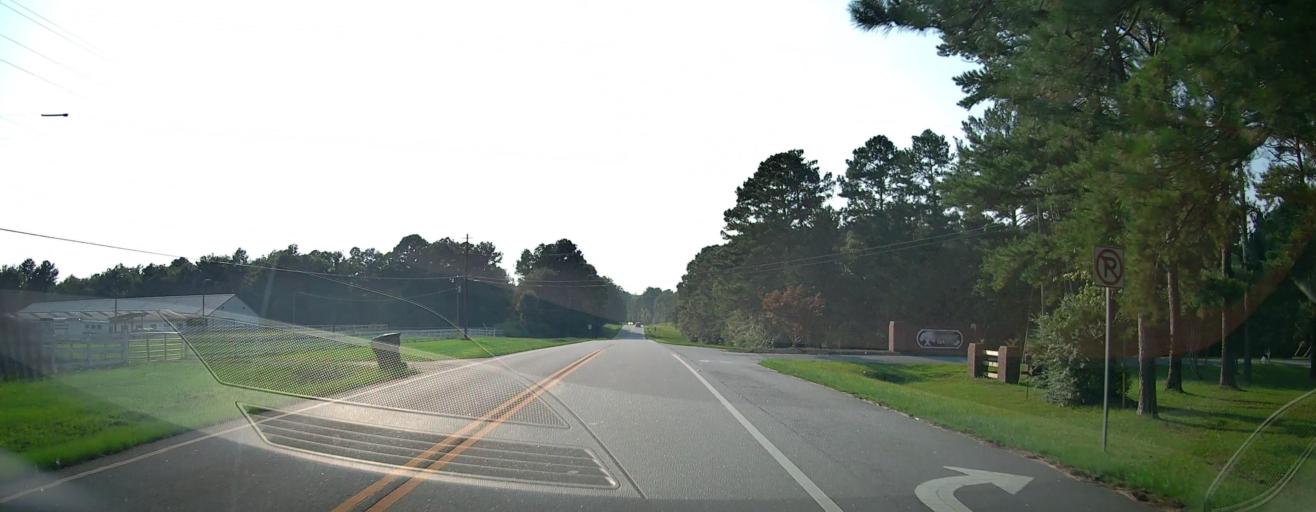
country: US
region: Georgia
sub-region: Bibb County
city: West Point
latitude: 32.8609
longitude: -83.8027
